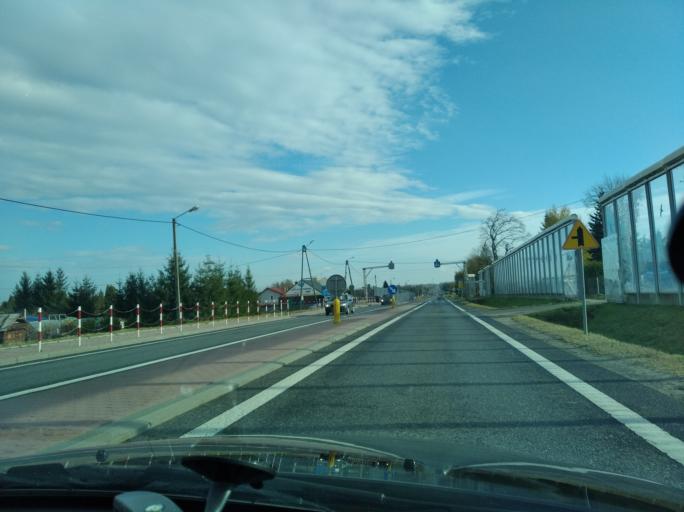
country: PL
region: Subcarpathian Voivodeship
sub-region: Powiat debicki
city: Brzeznica
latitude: 50.0623
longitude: 21.5268
